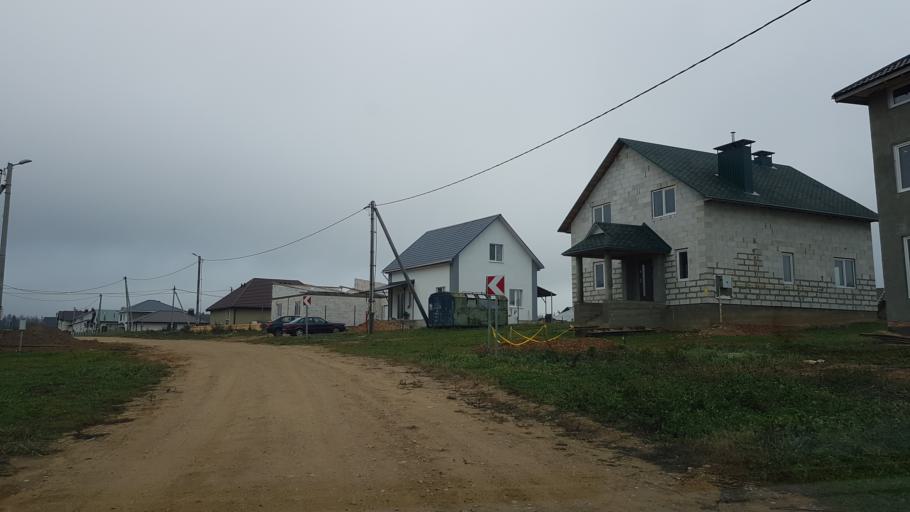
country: BY
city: Fanipol
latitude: 53.7261
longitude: 27.3259
